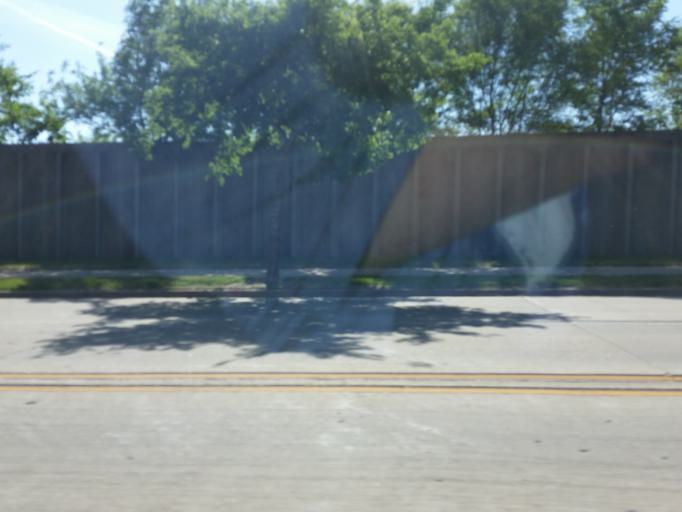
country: US
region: Wisconsin
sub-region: Rock County
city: Beloit
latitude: 42.5072
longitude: -89.0318
